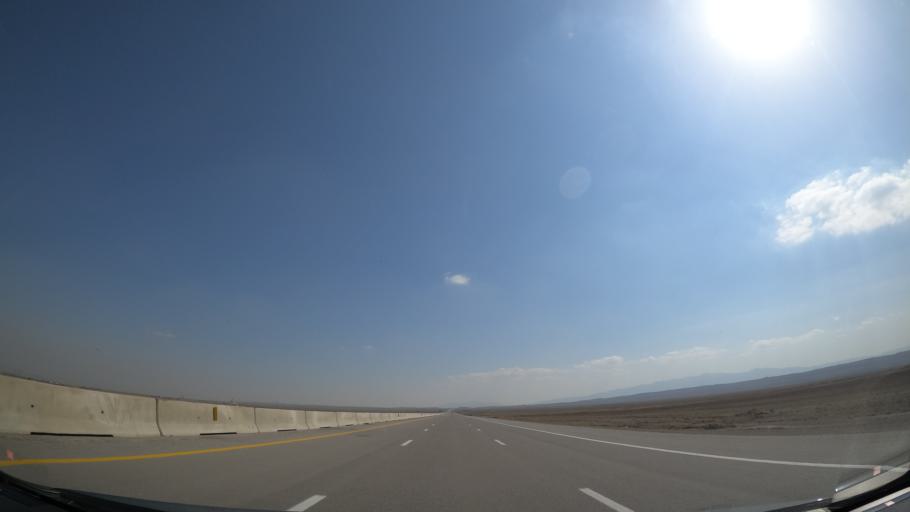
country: IR
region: Alborz
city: Nazarabad
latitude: 35.8336
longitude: 50.4966
